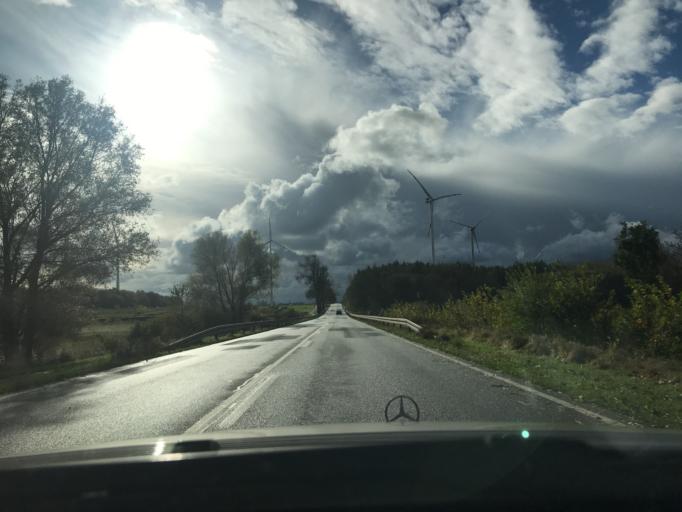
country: DE
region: Mecklenburg-Vorpommern
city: Jarmen
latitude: 53.8990
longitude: 13.3402
